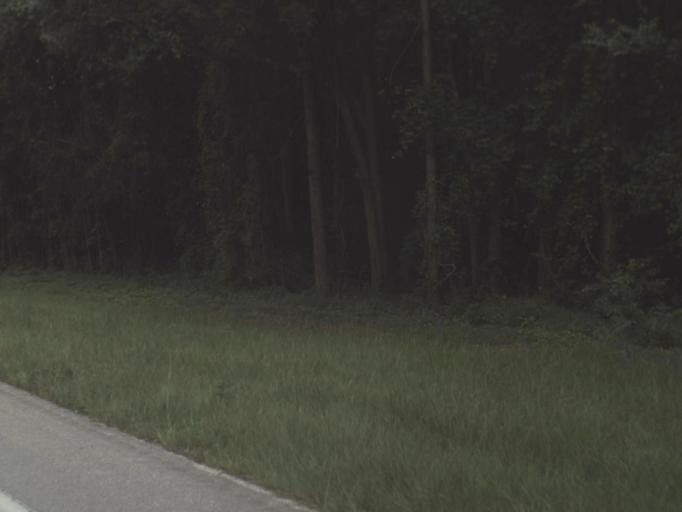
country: US
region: Florida
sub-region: Alachua County
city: Newberry
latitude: 29.7354
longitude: -82.6072
